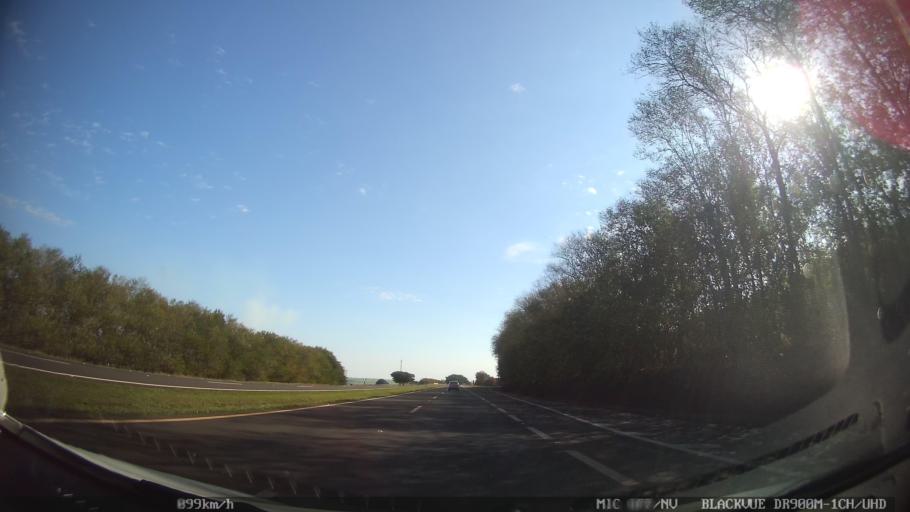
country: BR
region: Sao Paulo
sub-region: Iracemapolis
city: Iracemapolis
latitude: -22.6692
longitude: -47.5441
